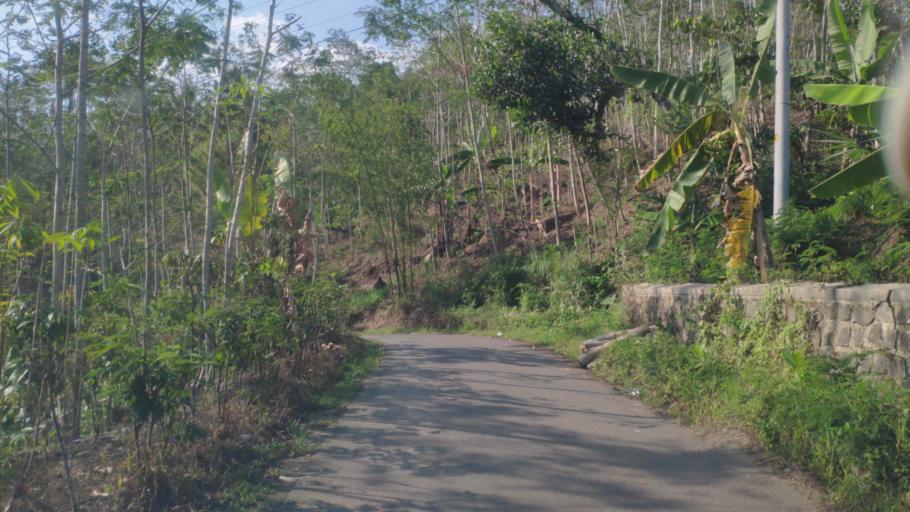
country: ID
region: Central Java
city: Buaran
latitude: -7.2427
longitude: 109.5890
